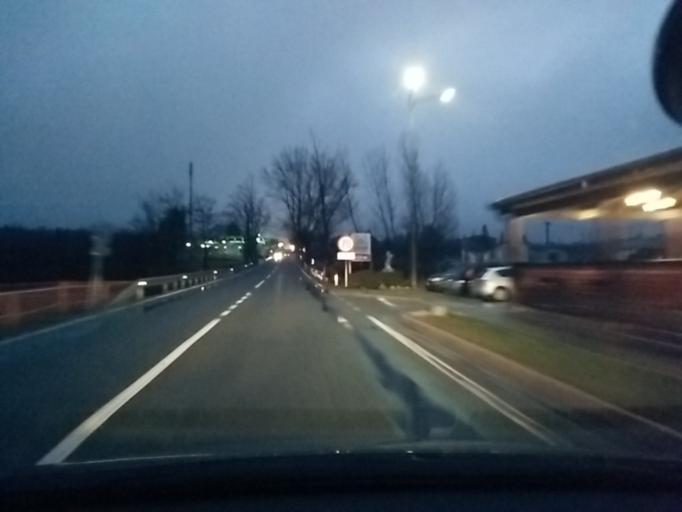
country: SI
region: Hrpelje-Kozina
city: Kozina
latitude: 45.6196
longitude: 13.9088
